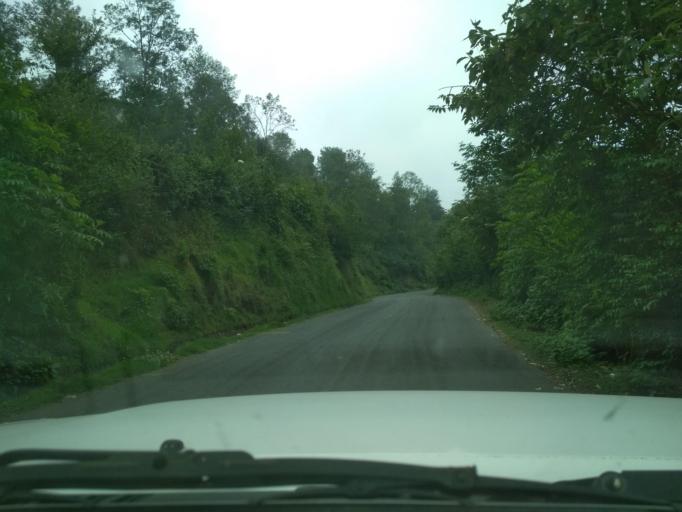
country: MX
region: Veracruz
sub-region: La Perla
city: Chilapa
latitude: 18.9666
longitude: -97.1716
